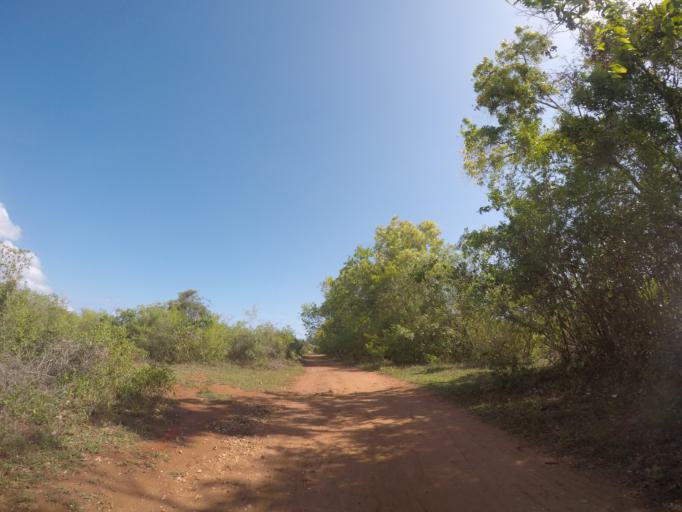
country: TZ
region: Zanzibar Central/South
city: Koani
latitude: -6.2114
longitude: 39.3000
